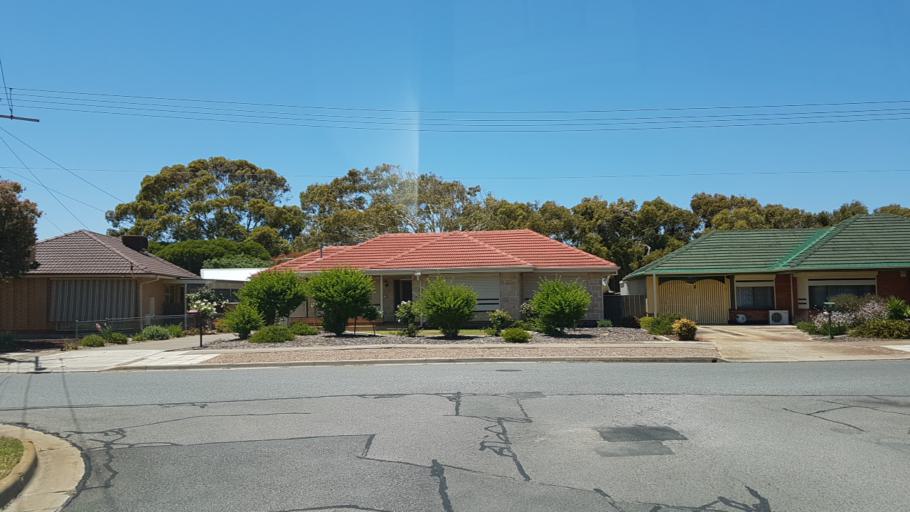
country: AU
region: South Australia
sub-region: Charles Sturt
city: West Lakes Shore
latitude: -34.8590
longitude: 138.4841
